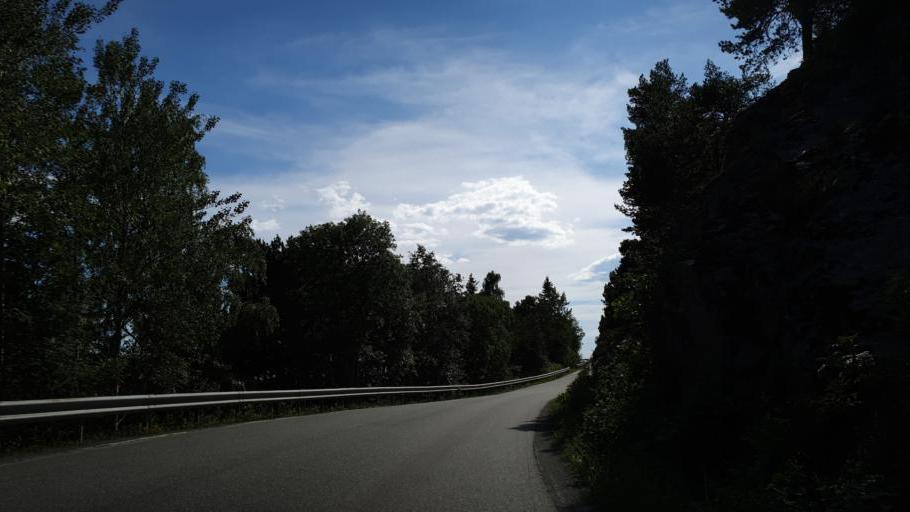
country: NO
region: Nord-Trondelag
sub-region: Leksvik
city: Leksvik
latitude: 63.6313
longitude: 10.5699
